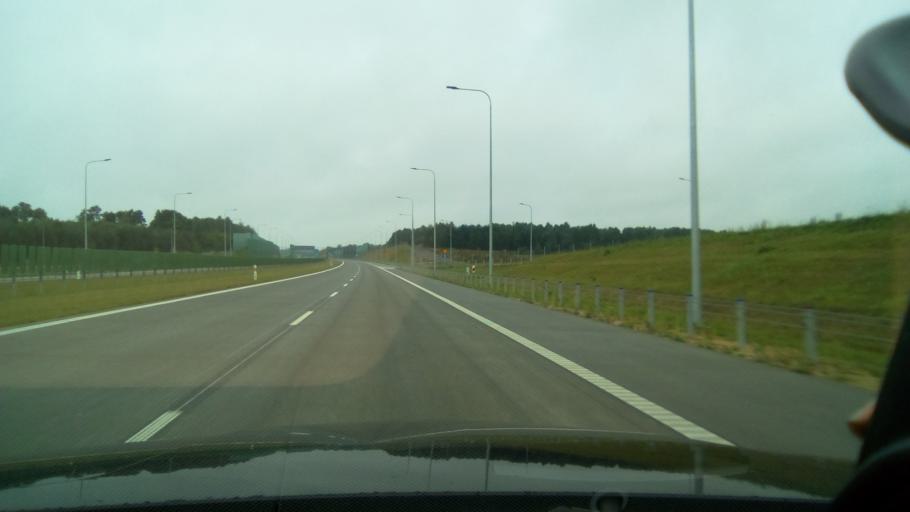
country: PL
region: Silesian Voivodeship
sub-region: Powiat klobucki
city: Kamyk
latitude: 50.8471
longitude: 19.0401
